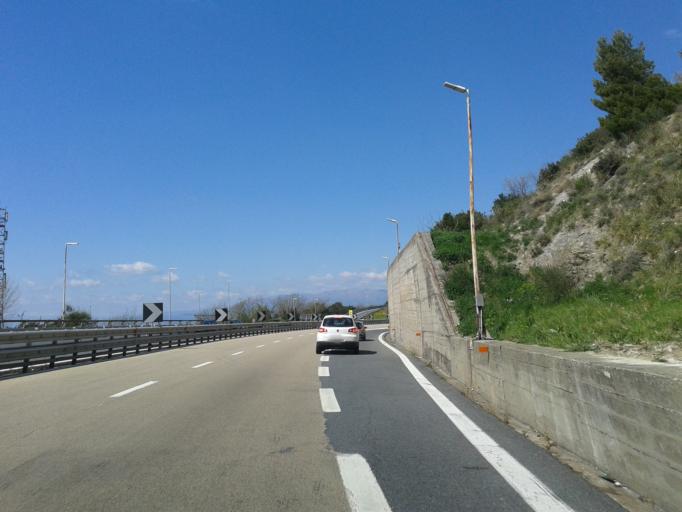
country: IT
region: Liguria
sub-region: Provincia di Genova
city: Bogliasco
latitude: 44.3955
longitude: 9.0113
